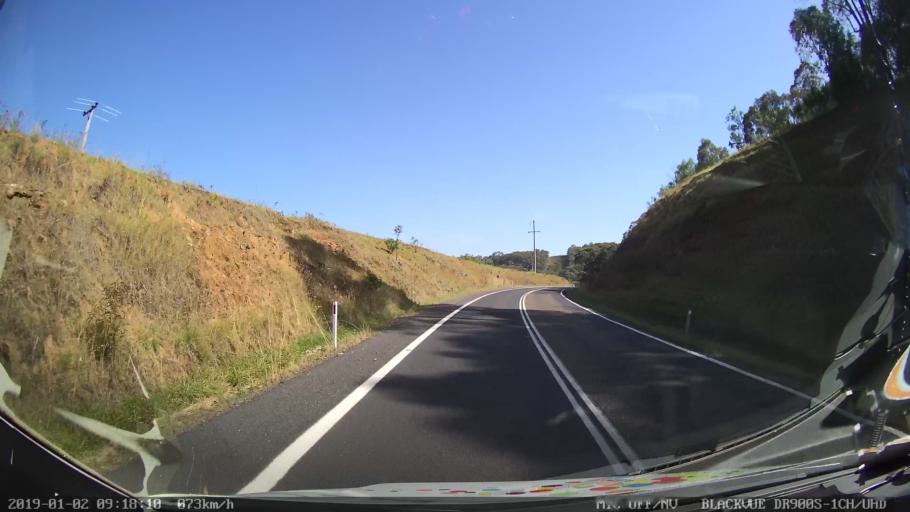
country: AU
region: New South Wales
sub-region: Tumut Shire
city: Tumut
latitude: -35.4319
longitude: 148.2853
